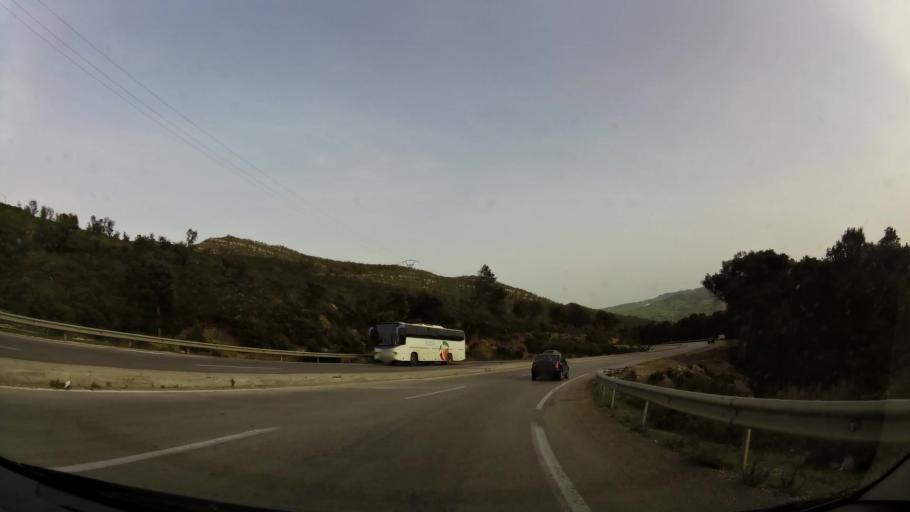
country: MA
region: Tanger-Tetouan
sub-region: Tetouan
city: Saddina
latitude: 35.5604
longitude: -5.5702
